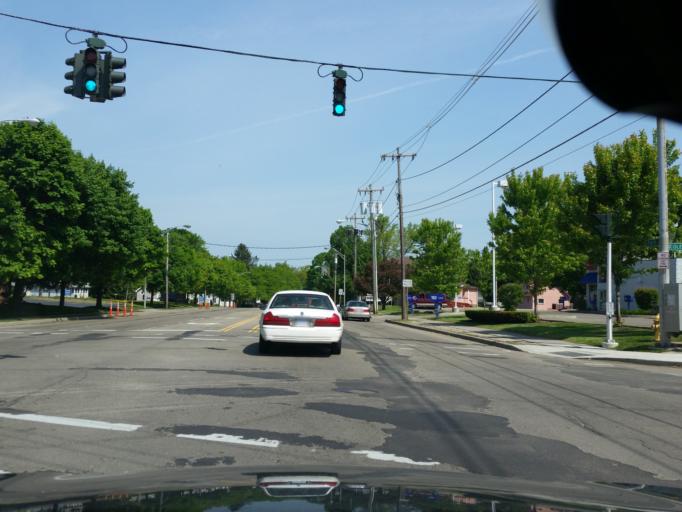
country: US
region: New York
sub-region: Chautauqua County
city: Jamestown
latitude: 42.0818
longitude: -79.2296
